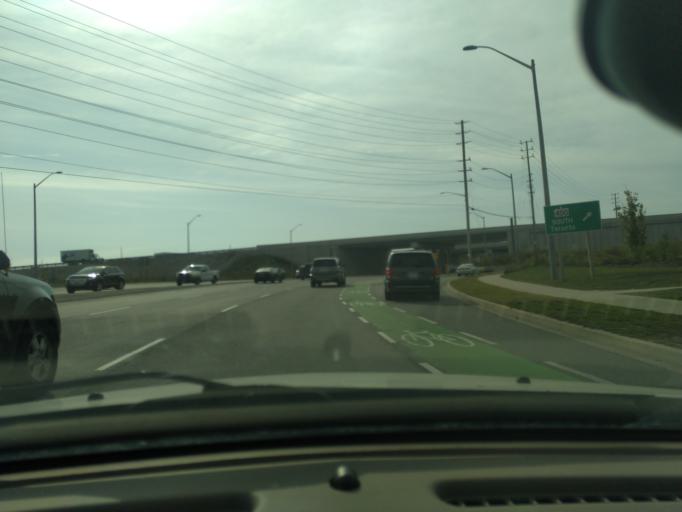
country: CA
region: Ontario
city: Barrie
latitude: 44.4155
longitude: -79.6734
